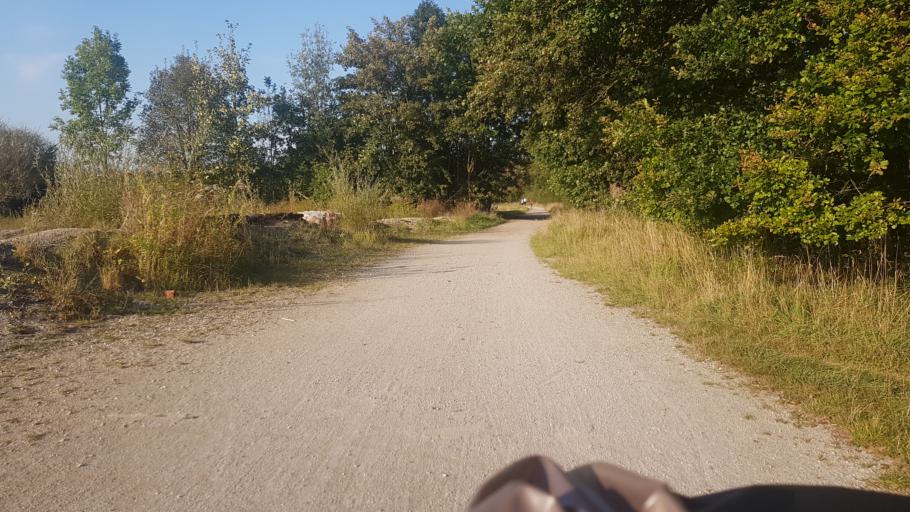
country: DE
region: Bavaria
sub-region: Upper Bavaria
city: Neubiberg
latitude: 48.0951
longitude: 11.6643
